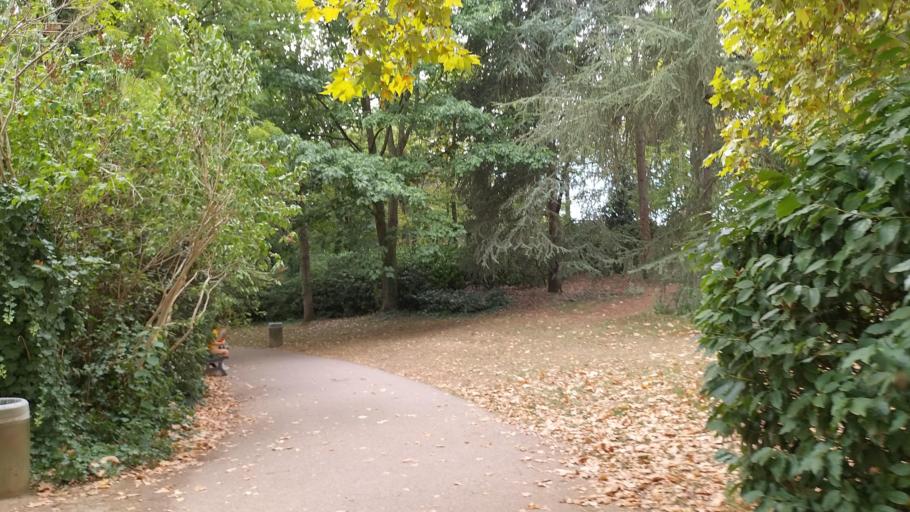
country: FR
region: Midi-Pyrenees
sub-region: Departement de la Haute-Garonne
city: Toulouse
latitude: 43.6114
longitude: 1.4335
